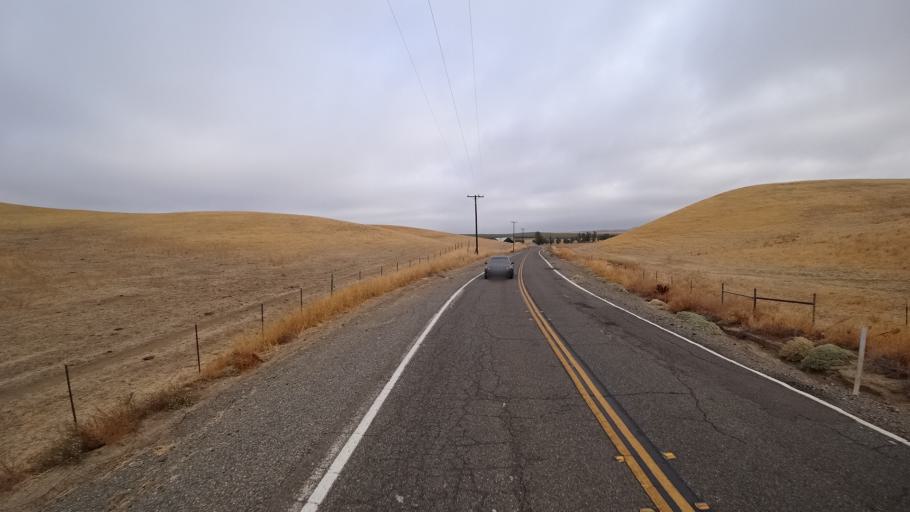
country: US
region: California
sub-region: Yolo County
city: Dunnigan
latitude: 38.8576
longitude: -122.0456
